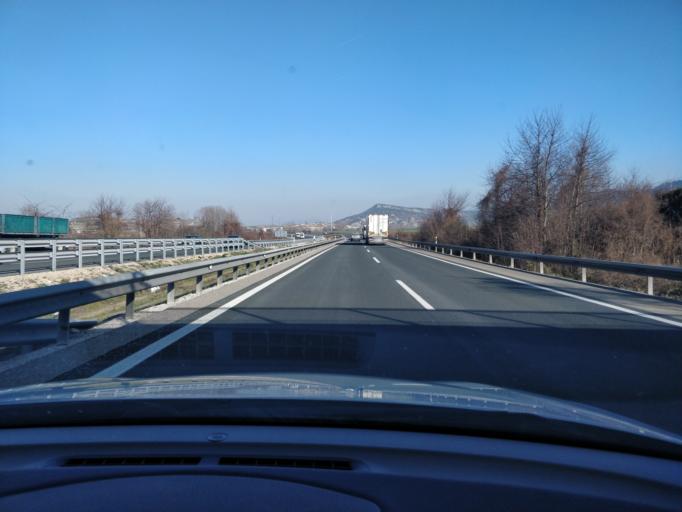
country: ES
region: Castille and Leon
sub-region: Provincia de Burgos
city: Ameyugo
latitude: 42.6555
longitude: -3.0564
